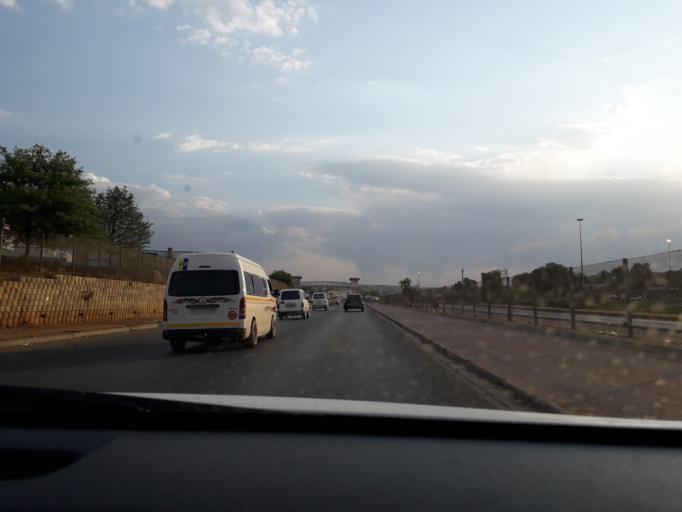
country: ZA
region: Gauteng
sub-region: Ekurhuleni Metropolitan Municipality
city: Tembisa
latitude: -26.0253
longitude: 28.1961
